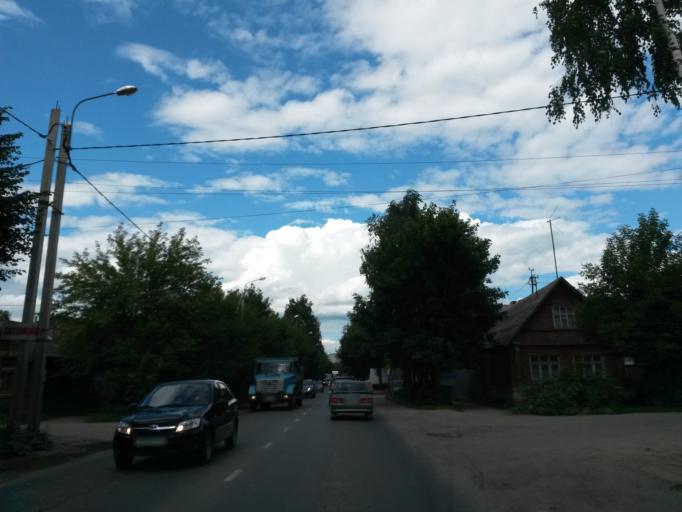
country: RU
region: Ivanovo
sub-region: Gorod Ivanovo
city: Ivanovo
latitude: 56.9900
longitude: 40.9529
